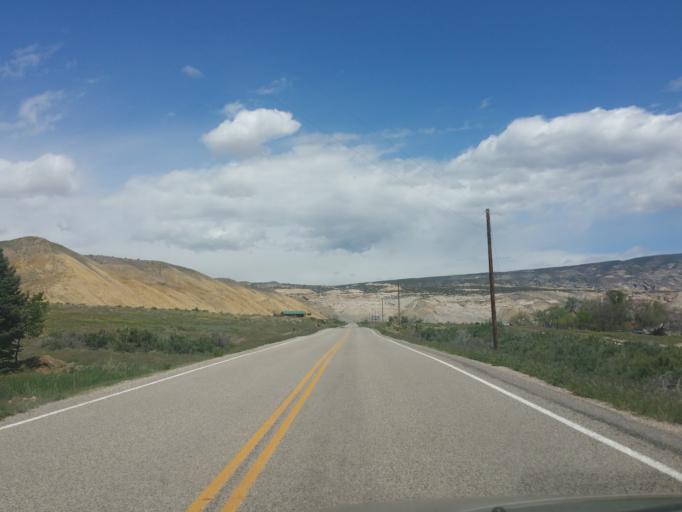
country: US
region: Utah
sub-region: Uintah County
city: Naples
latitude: 40.4192
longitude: -109.3381
